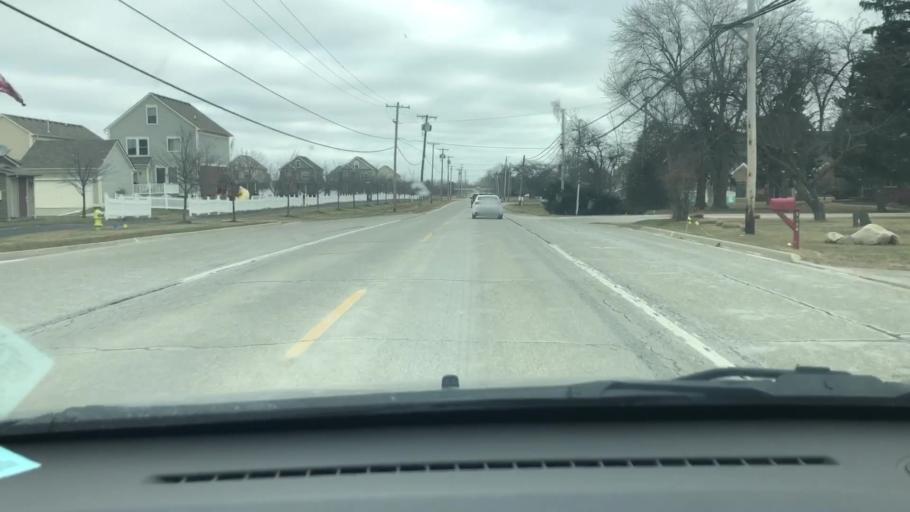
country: US
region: Michigan
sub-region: Macomb County
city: Shelby
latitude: 42.7282
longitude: -83.0324
